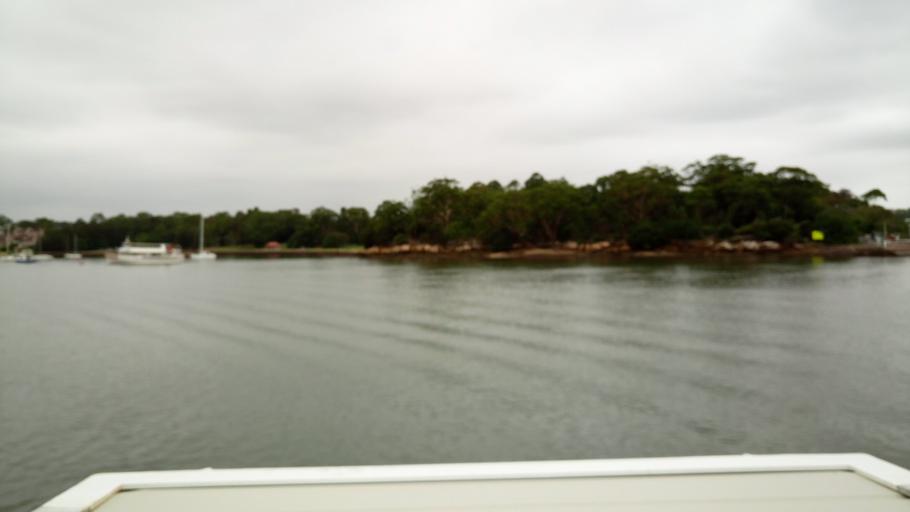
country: AU
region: New South Wales
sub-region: Canada Bay
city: Concord
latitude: -33.8360
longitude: 151.1066
